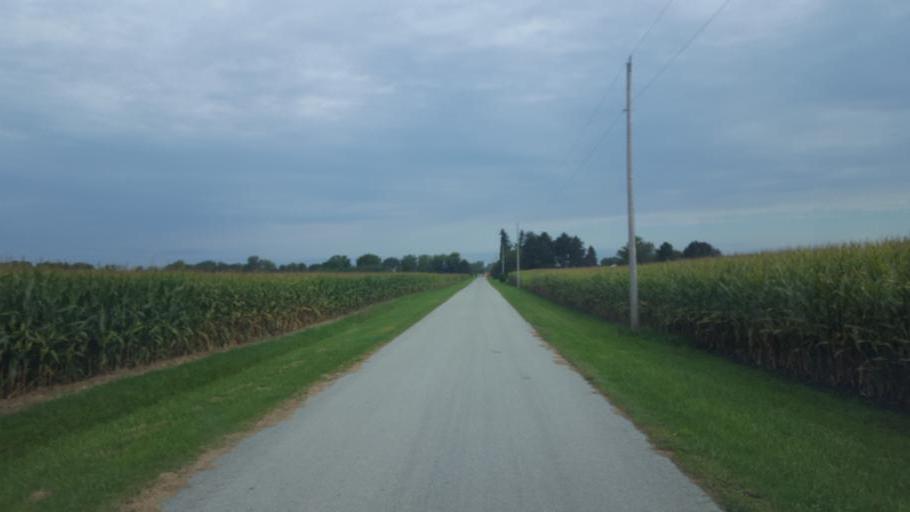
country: US
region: Ohio
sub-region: Wyandot County
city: Upper Sandusky
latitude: 40.7628
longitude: -83.1690
